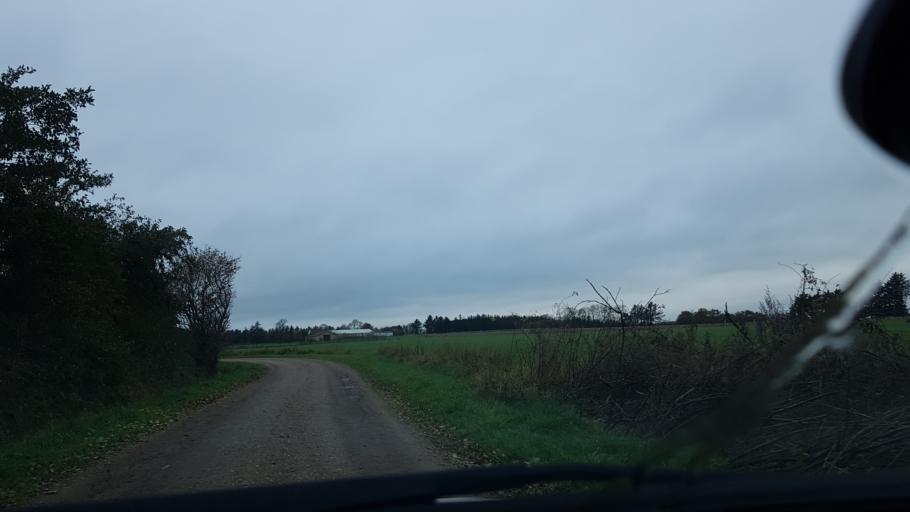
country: DK
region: South Denmark
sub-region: Esbjerg Kommune
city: Ribe
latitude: 55.2806
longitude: 8.8484
